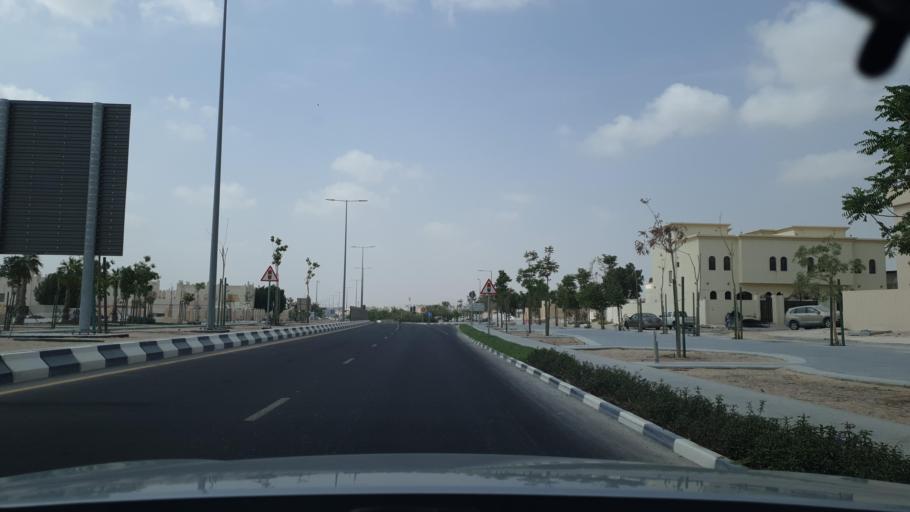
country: QA
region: Baladiyat ar Rayyan
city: Ar Rayyan
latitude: 25.2776
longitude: 51.4584
